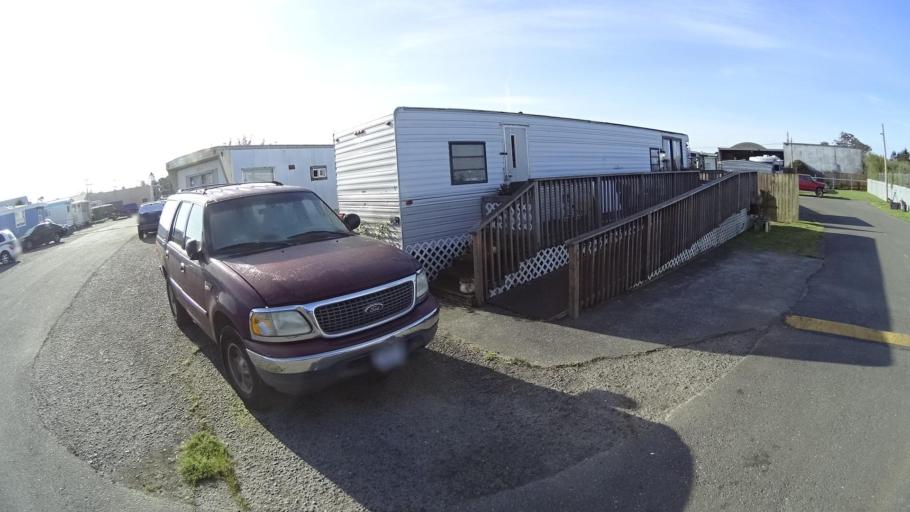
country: US
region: California
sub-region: Humboldt County
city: Bayview
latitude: 40.7745
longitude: -124.1938
